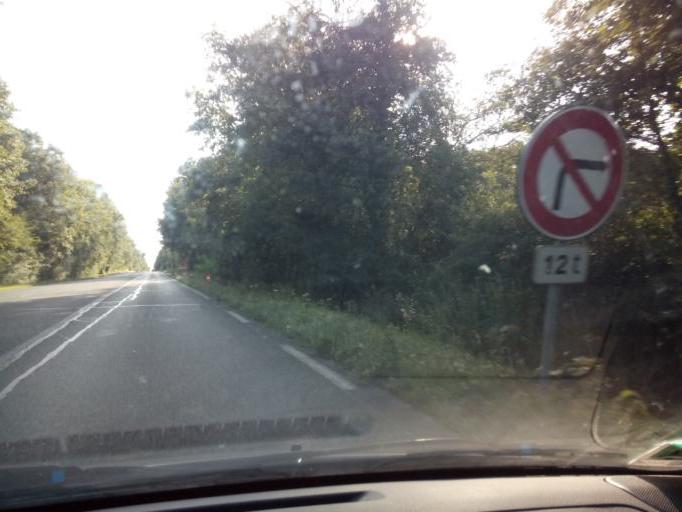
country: FR
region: Centre
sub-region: Departement d'Indre-et-Loire
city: Sache
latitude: 47.2896
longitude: 0.5262
